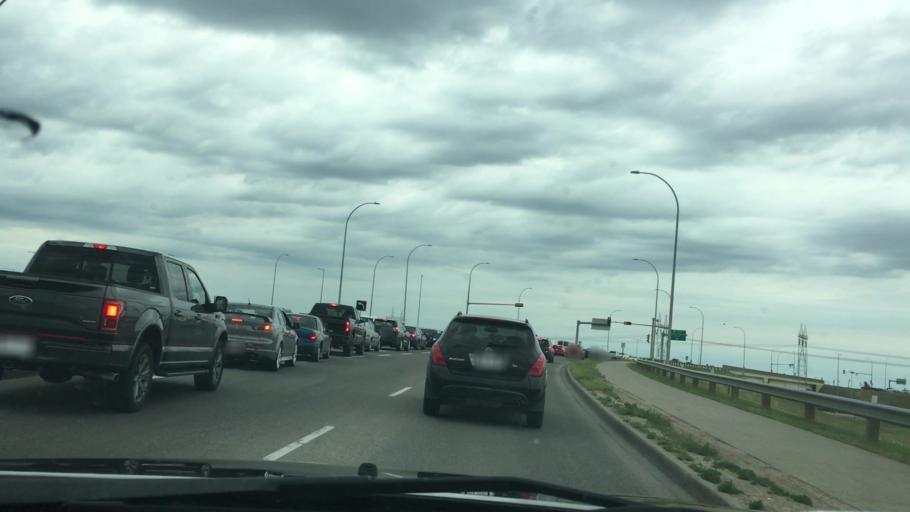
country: CA
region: Alberta
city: Edmonton
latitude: 53.4321
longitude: -113.5182
